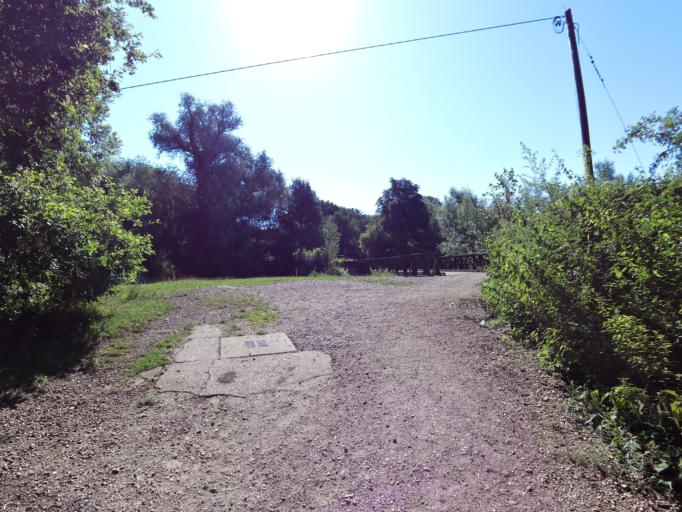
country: DE
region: North Rhine-Westphalia
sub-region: Regierungsbezirk Koln
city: Wurselen
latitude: 50.8101
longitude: 6.1050
